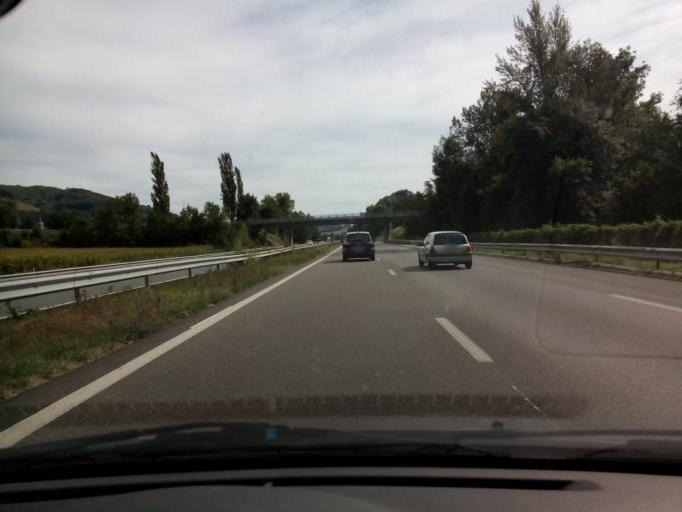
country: FR
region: Rhone-Alpes
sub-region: Departement de l'Isere
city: Chabons
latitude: 45.4865
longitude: 5.3986
